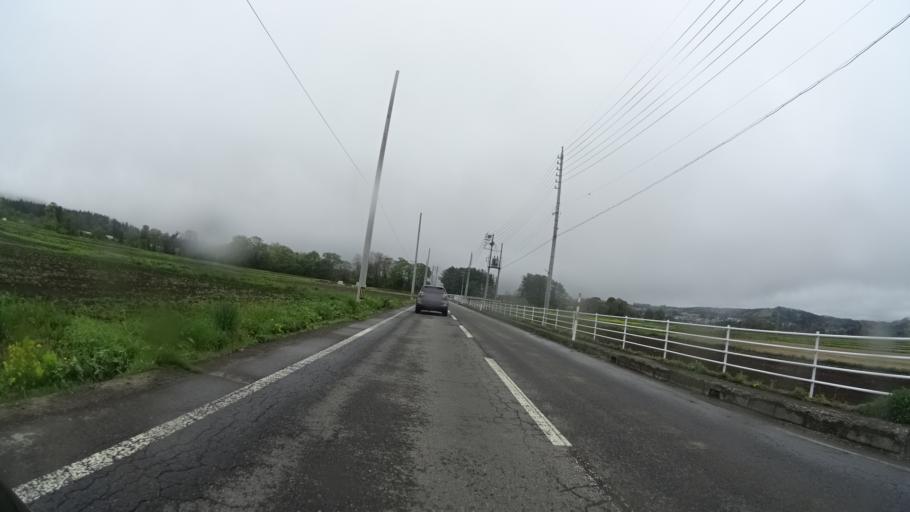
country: JP
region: Nagano
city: Nagano-shi
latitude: 36.7911
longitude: 138.1963
